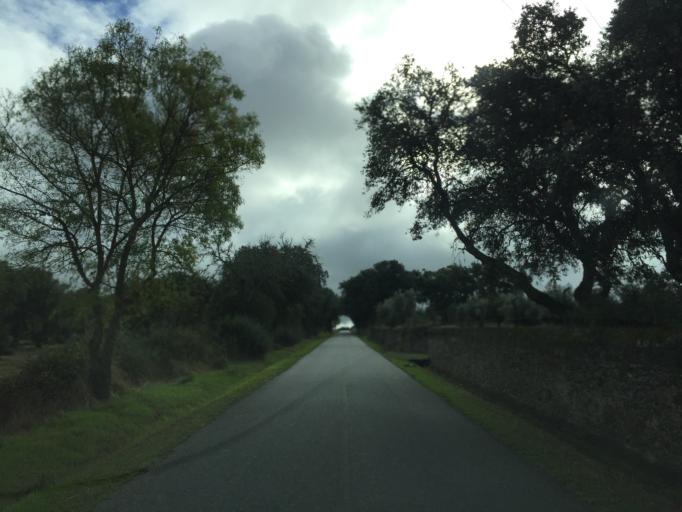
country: PT
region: Portalegre
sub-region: Alter do Chao
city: Alter do Chao
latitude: 39.2280
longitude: -7.6808
